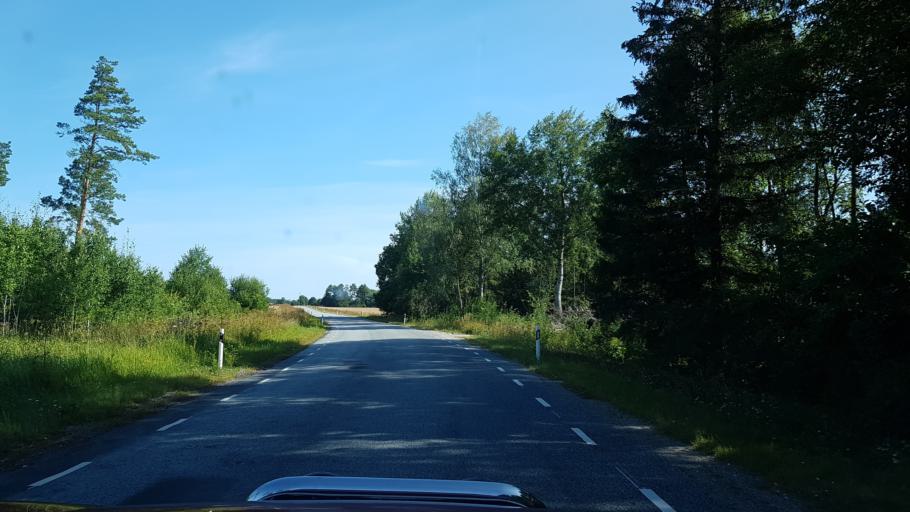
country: EE
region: Harju
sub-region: Raasiku vald
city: Raasiku
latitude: 59.2893
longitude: 25.1671
